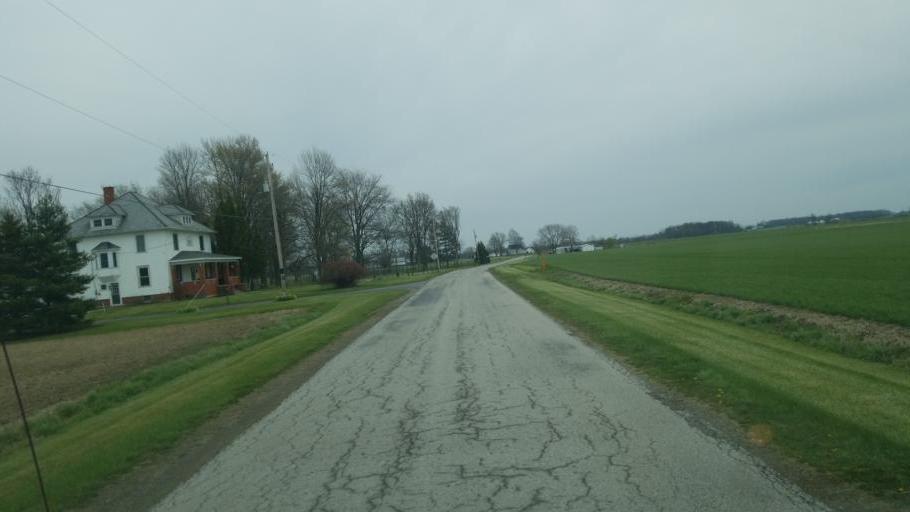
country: US
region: Ohio
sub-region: Wyandot County
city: Carey
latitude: 40.9756
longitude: -83.5110
